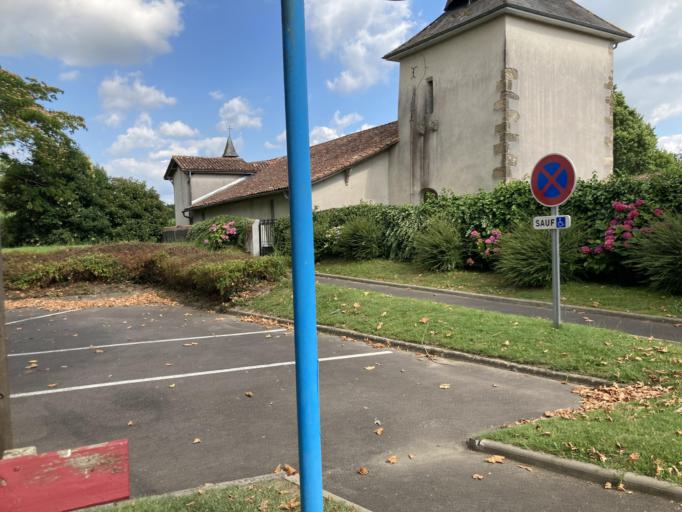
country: FR
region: Aquitaine
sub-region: Departement des Landes
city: Hinx
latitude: 43.7559
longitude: -0.8921
